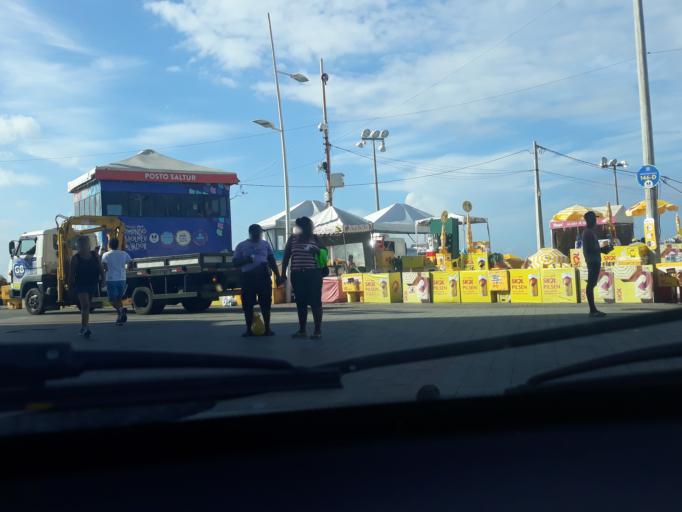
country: BR
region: Bahia
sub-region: Salvador
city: Salvador
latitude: -13.0098
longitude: -38.5320
